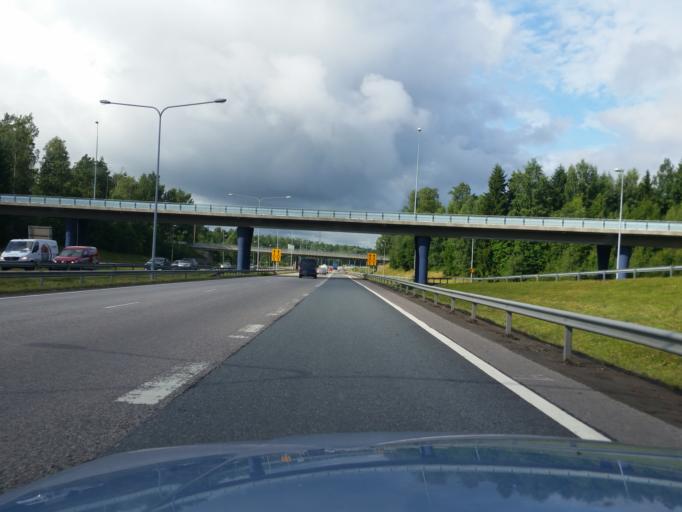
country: FI
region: Uusimaa
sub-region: Helsinki
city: Kauniainen
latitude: 60.2044
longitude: 24.7448
